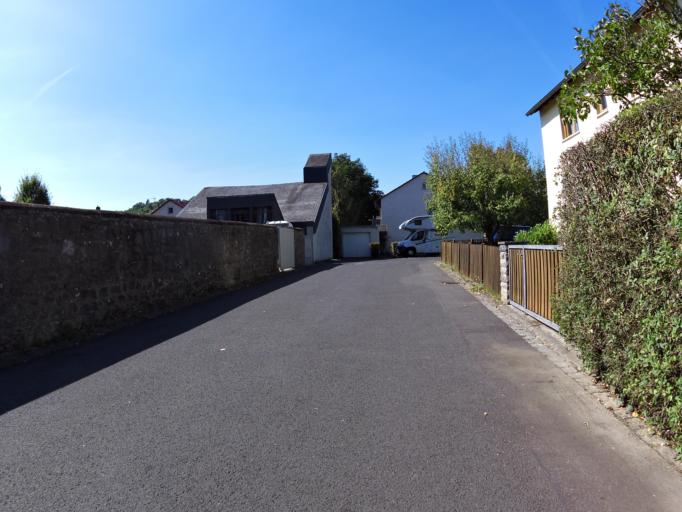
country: DE
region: Bavaria
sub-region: Regierungsbezirk Unterfranken
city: Margetshochheim
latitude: 49.8395
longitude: 9.8654
